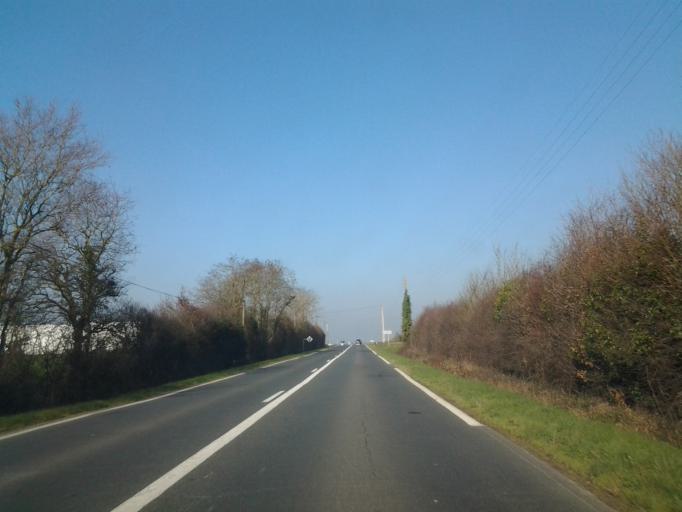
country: FR
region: Pays de la Loire
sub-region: Departement de la Vendee
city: Mache
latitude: 46.7872
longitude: -1.6999
